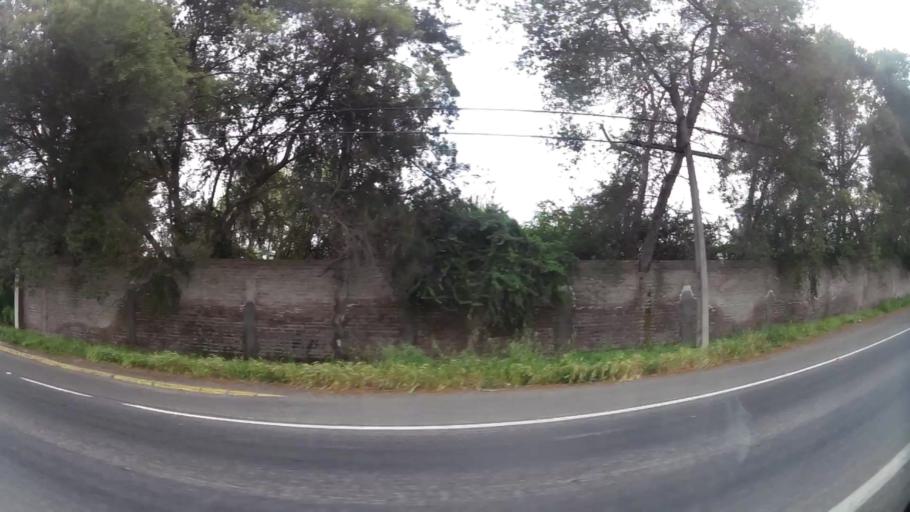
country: CL
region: Santiago Metropolitan
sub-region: Provincia de Chacabuco
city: Chicureo Abajo
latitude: -33.2483
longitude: -70.7128
